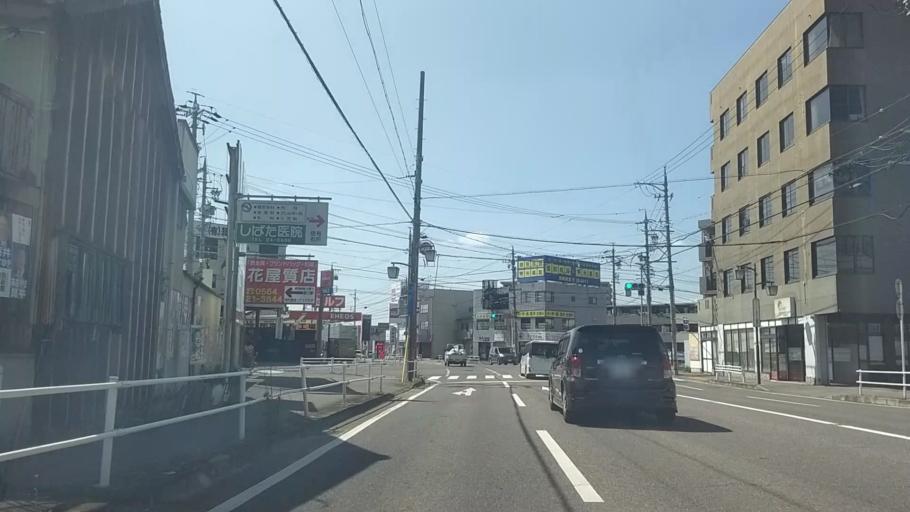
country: JP
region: Aichi
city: Okazaki
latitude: 34.9713
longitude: 137.1713
